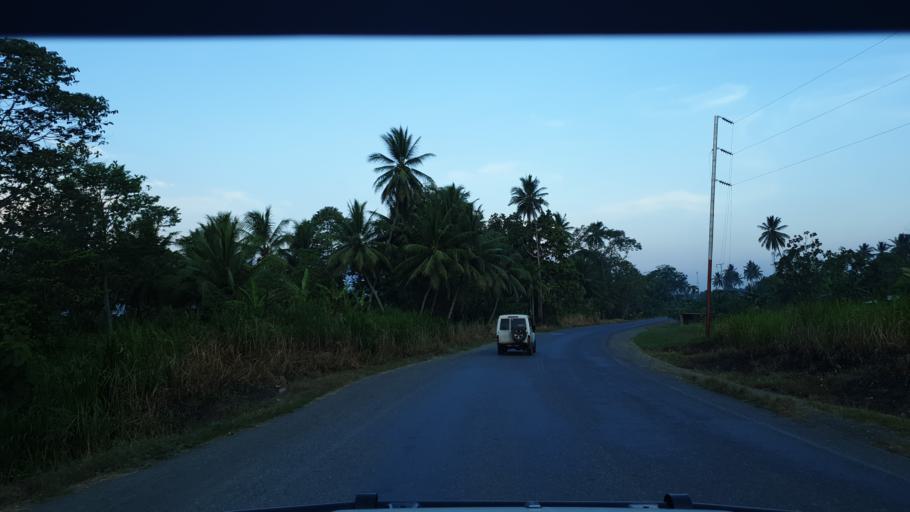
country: PG
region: Morobe
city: Lae
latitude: -6.5955
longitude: 146.7880
